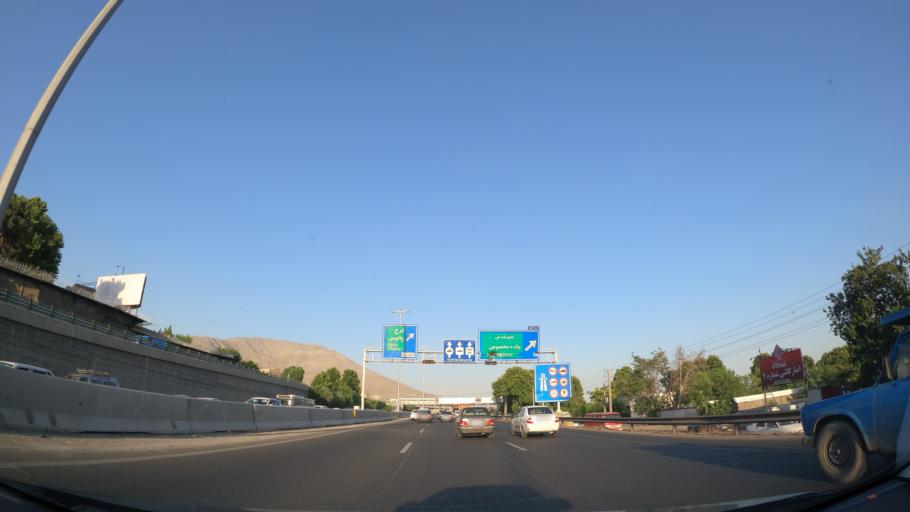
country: IR
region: Alborz
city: Karaj
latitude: 35.7894
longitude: 51.0165
